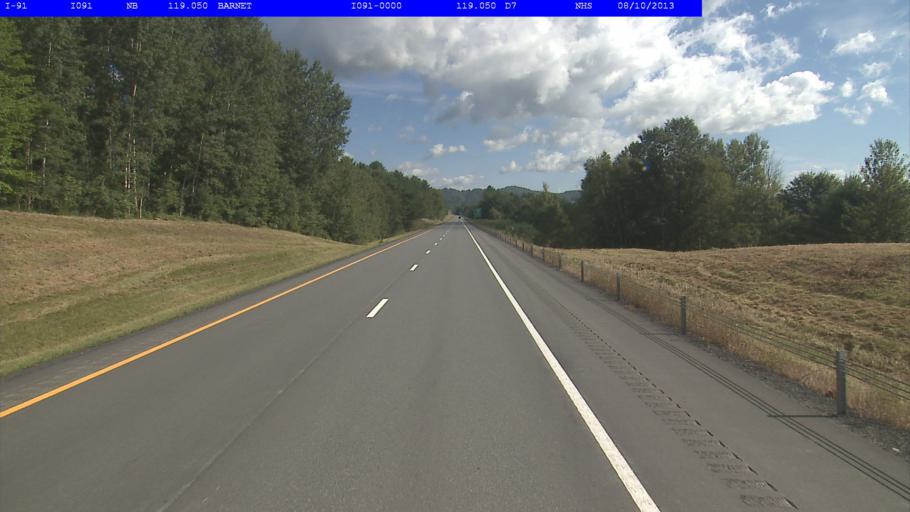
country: US
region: New Hampshire
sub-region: Grafton County
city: Woodsville
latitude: 44.2802
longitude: -72.0689
